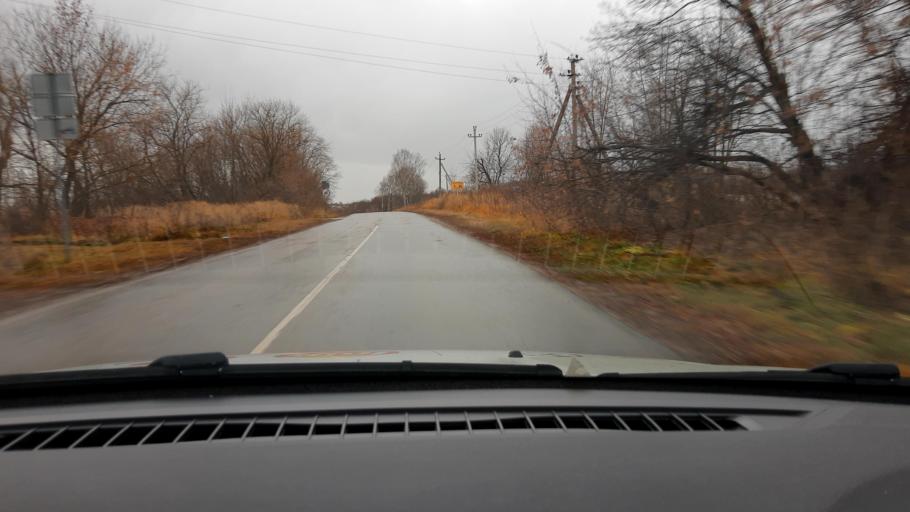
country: RU
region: Nizjnij Novgorod
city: Bogorodsk
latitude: 56.1788
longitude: 43.5003
